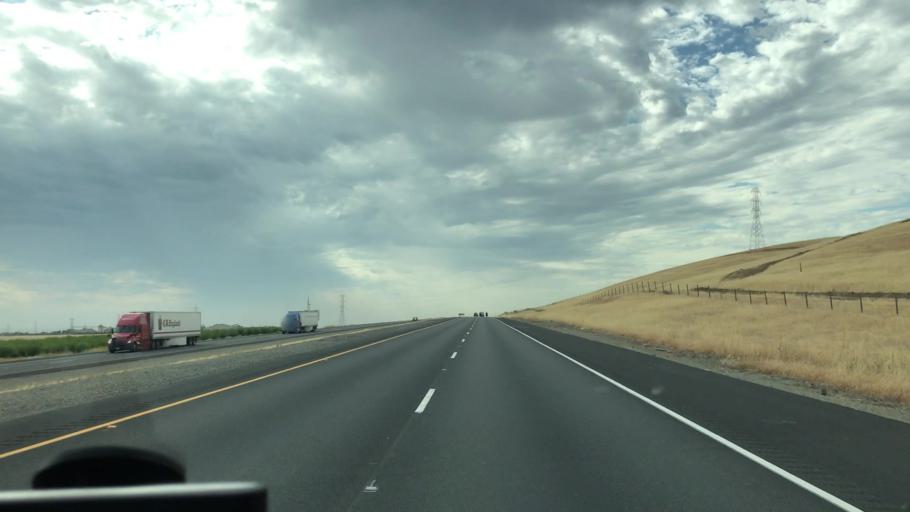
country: US
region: California
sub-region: San Joaquin County
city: Tracy
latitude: 37.6271
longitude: -121.3833
